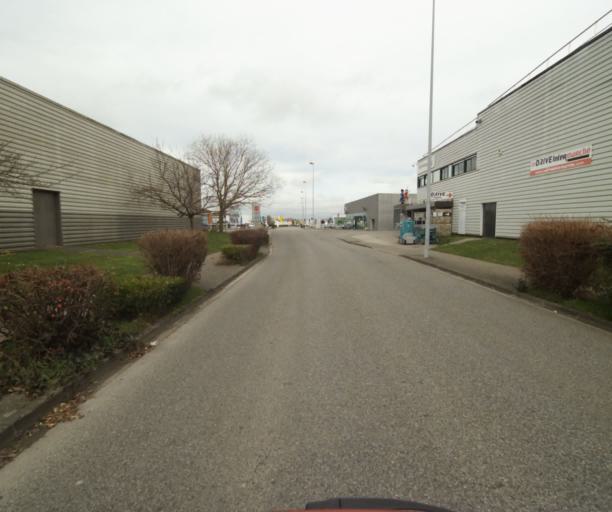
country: FR
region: Midi-Pyrenees
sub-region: Departement de l'Ariege
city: Saint-Jean-du-Falga
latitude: 43.1059
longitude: 1.6303
